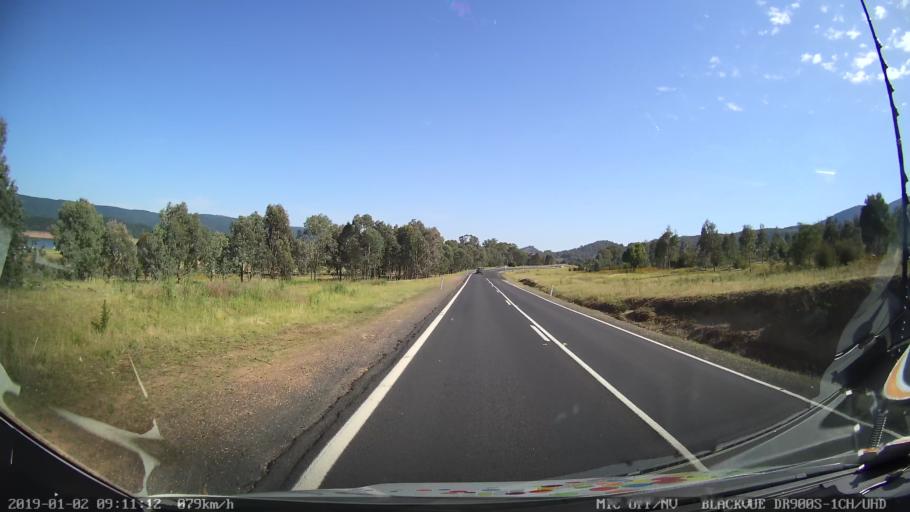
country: AU
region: New South Wales
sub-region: Tumut Shire
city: Tumut
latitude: -35.5138
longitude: 148.2688
